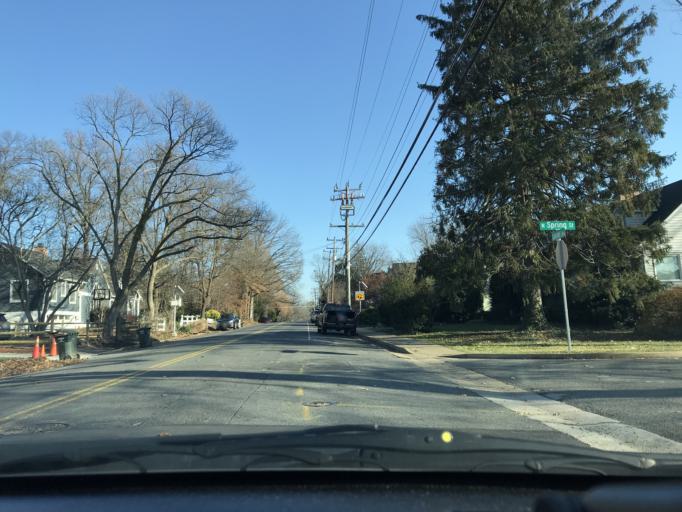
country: US
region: Virginia
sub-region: City of Falls Church
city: Falls Church
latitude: 38.8918
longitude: -77.1795
